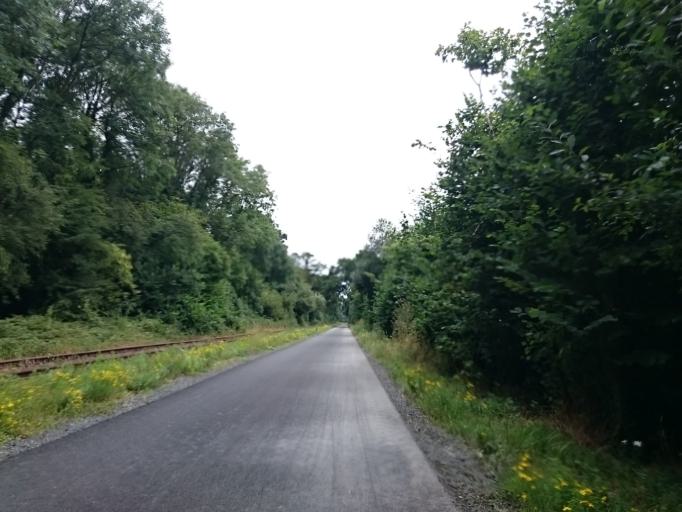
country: FR
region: Lower Normandy
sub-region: Departement du Calvados
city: Sainte-Honorine-du-Fay
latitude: 49.0411
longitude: -0.4634
